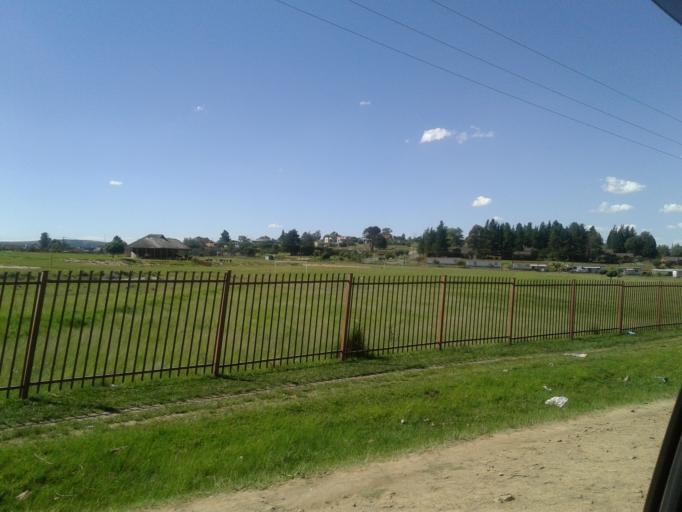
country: LS
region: Butha-Buthe
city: Butha-Buthe
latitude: -28.7600
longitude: 28.2569
